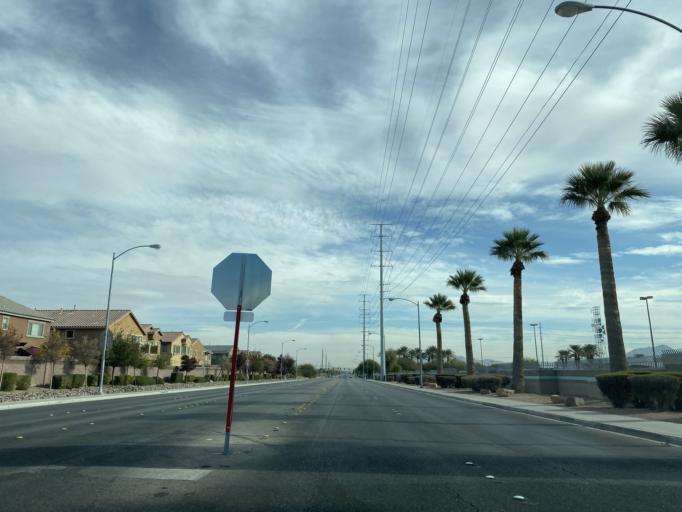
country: US
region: Nevada
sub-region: Clark County
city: North Las Vegas
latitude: 36.2469
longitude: -115.1214
